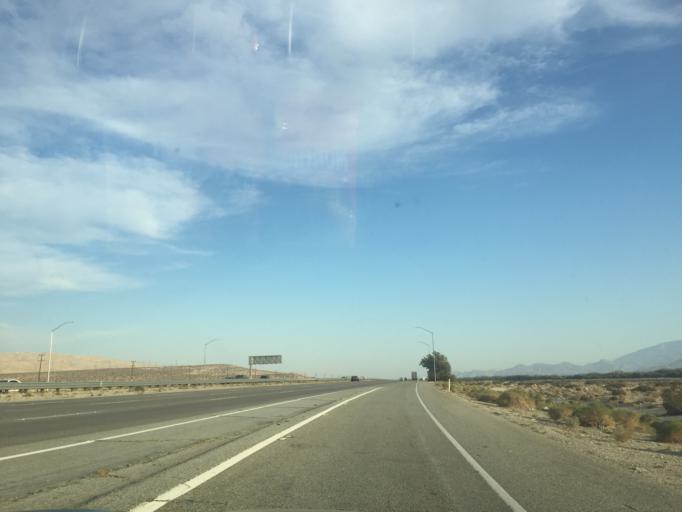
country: US
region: California
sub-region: Riverside County
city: Garnet
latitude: 33.8775
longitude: -116.5017
